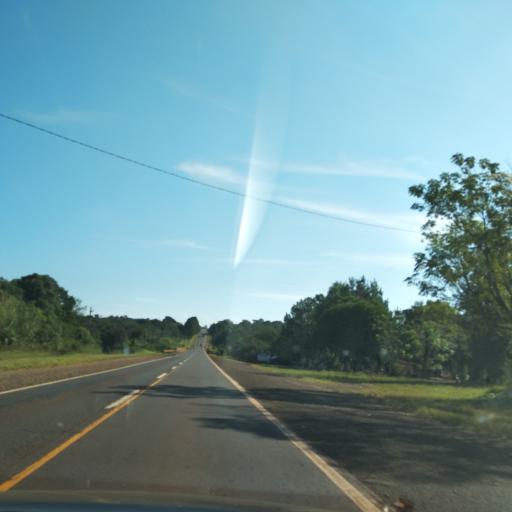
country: AR
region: Misiones
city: Santo Pipo
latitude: -27.1198
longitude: -55.3718
